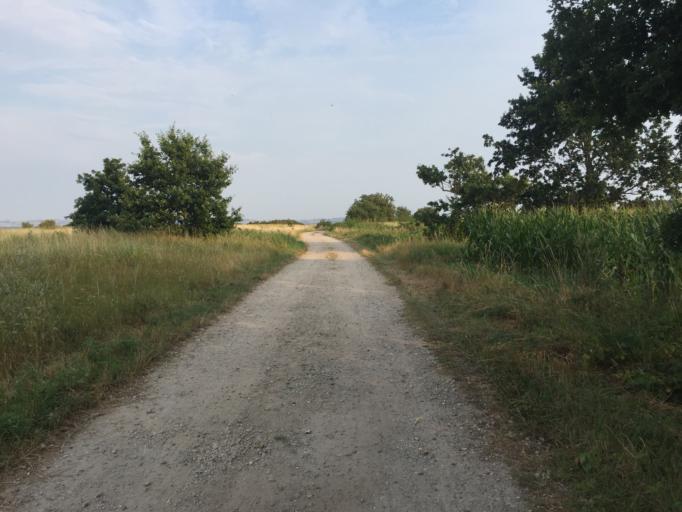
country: DK
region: South Denmark
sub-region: Assens Kommune
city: Harby
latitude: 55.1328
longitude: 10.0416
